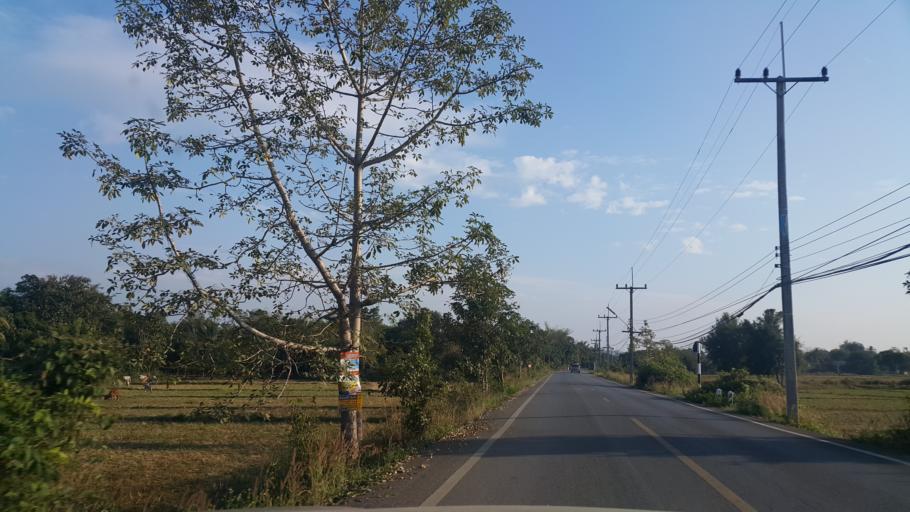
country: TH
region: Lampang
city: Soem Ngam
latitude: 18.1036
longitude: 99.3383
